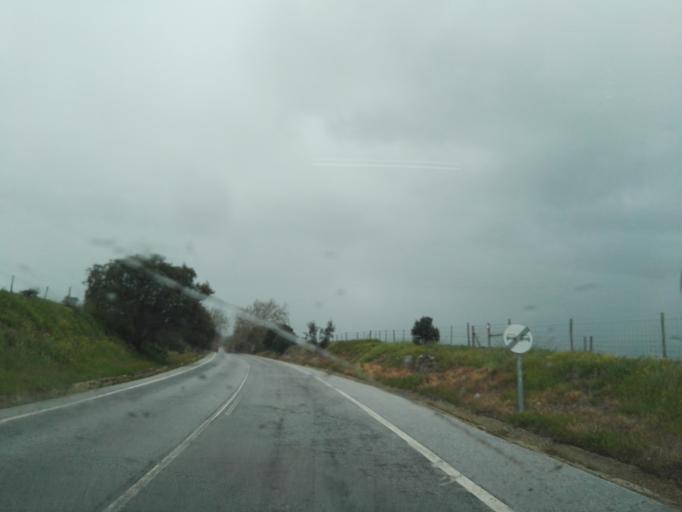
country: PT
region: Portalegre
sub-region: Arronches
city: Arronches
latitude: 39.0375
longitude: -7.2586
